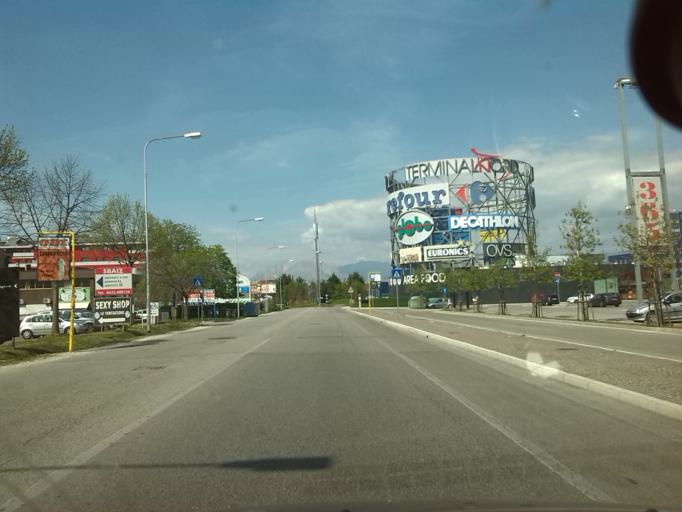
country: IT
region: Friuli Venezia Giulia
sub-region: Provincia di Udine
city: Feletto Umberto
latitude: 46.0926
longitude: 13.2318
